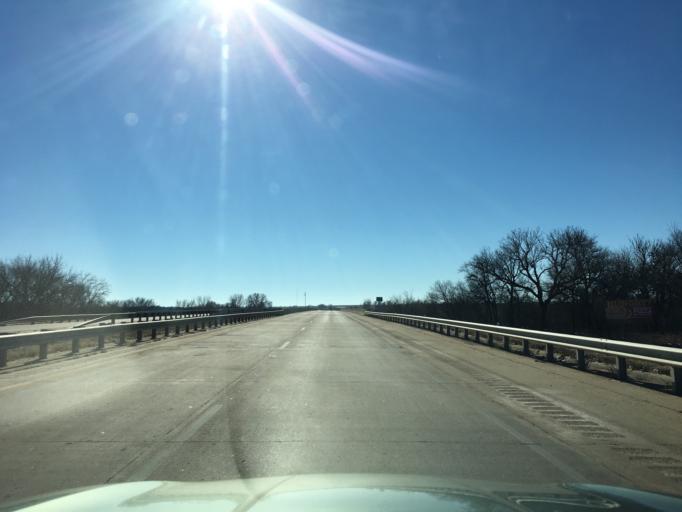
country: US
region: Oklahoma
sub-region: Kay County
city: Blackwell
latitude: 36.9096
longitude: -97.3527
